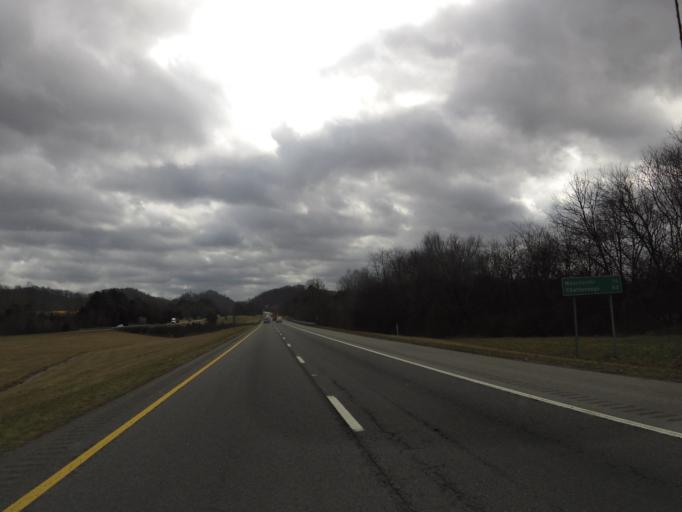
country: US
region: Tennessee
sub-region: Rutherford County
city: Plainview
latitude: 35.6098
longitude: -86.2406
